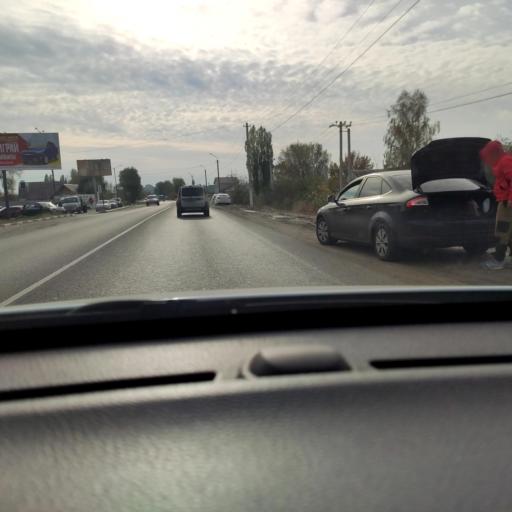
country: RU
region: Voronezj
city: Novaya Usman'
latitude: 51.6218
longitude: 39.3972
